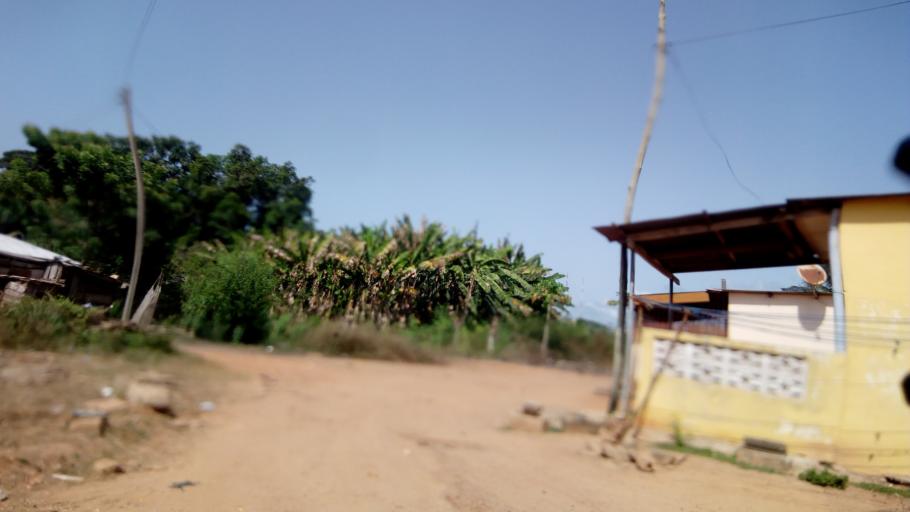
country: GH
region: Central
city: Cape Coast
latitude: 5.1124
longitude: -1.2667
